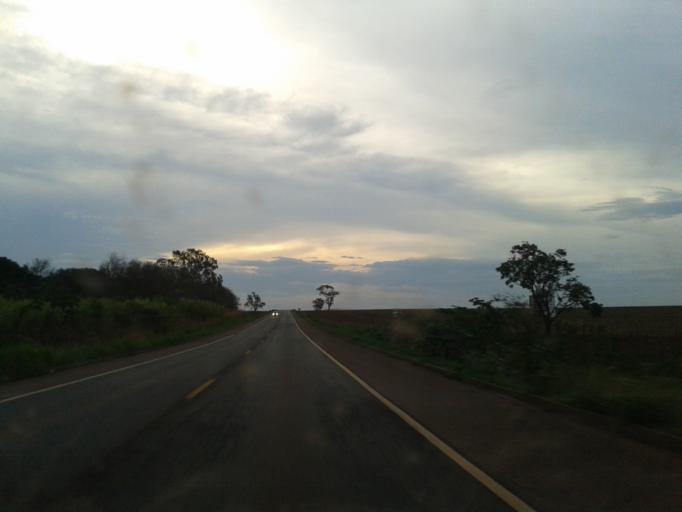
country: BR
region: Goias
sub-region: Santa Helena De Goias
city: Santa Helena de Goias
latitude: -17.8875
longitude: -50.6769
